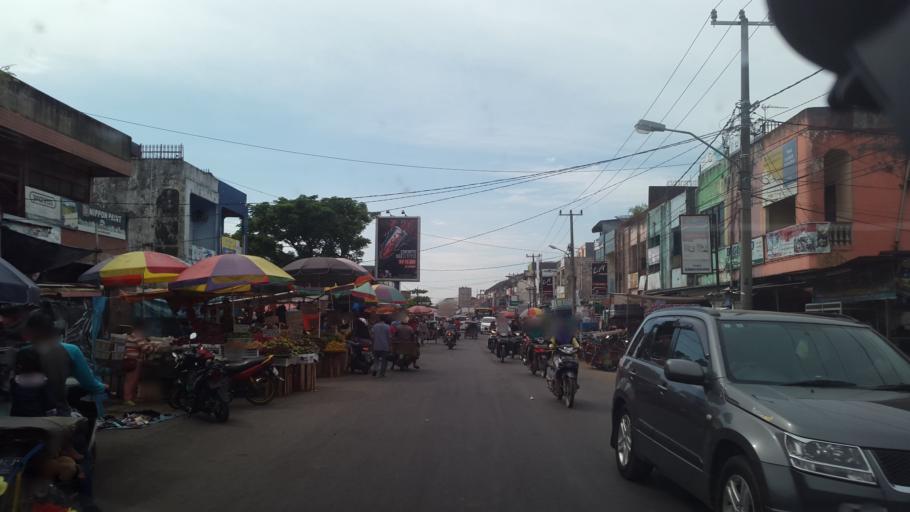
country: ID
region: South Sumatra
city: Plaju
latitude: -2.9970
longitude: 104.8152
